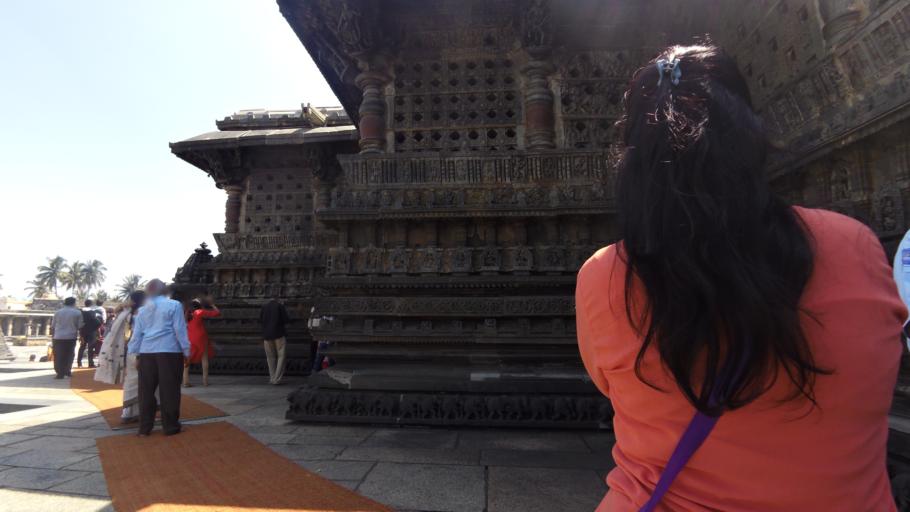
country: IN
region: Karnataka
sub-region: Hassan
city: Belur
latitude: 13.1630
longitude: 75.8603
